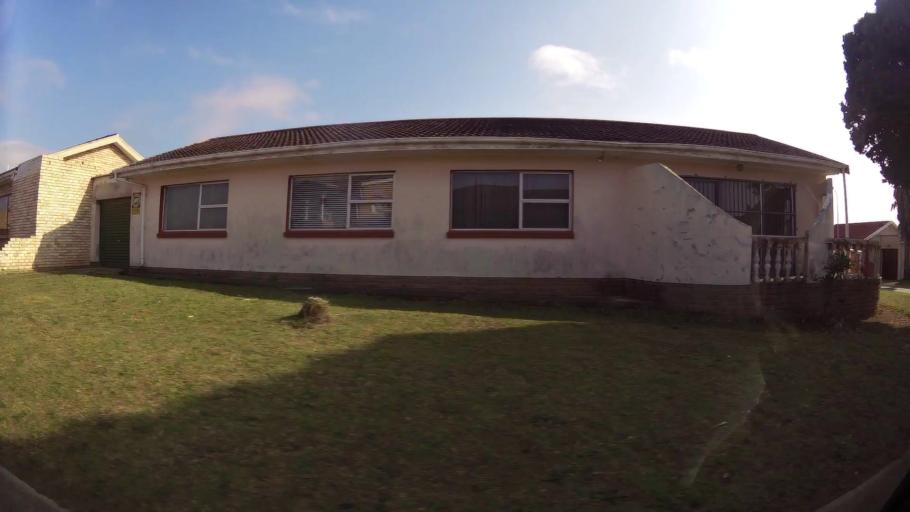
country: ZA
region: Eastern Cape
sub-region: Nelson Mandela Bay Metropolitan Municipality
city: Port Elizabeth
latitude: -33.9246
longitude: 25.5325
